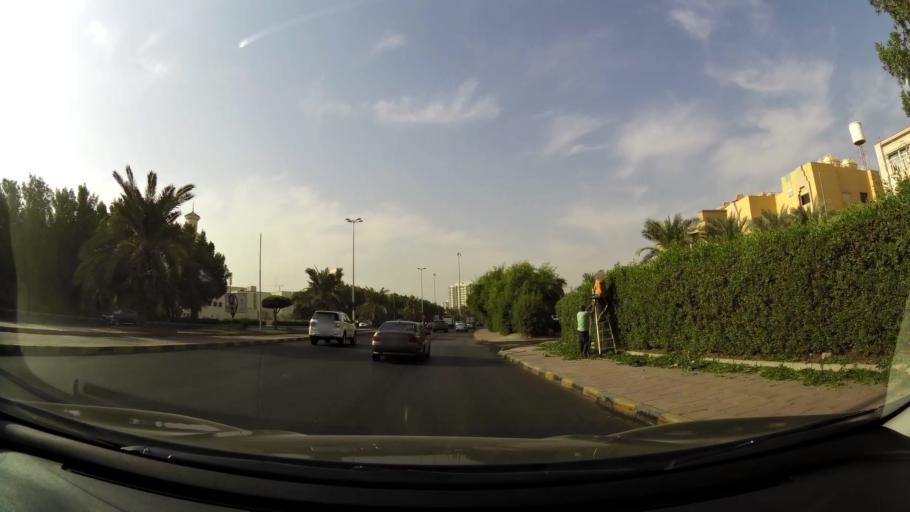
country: KW
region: Muhafazat Hawalli
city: Salwa
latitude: 29.2718
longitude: 48.0881
